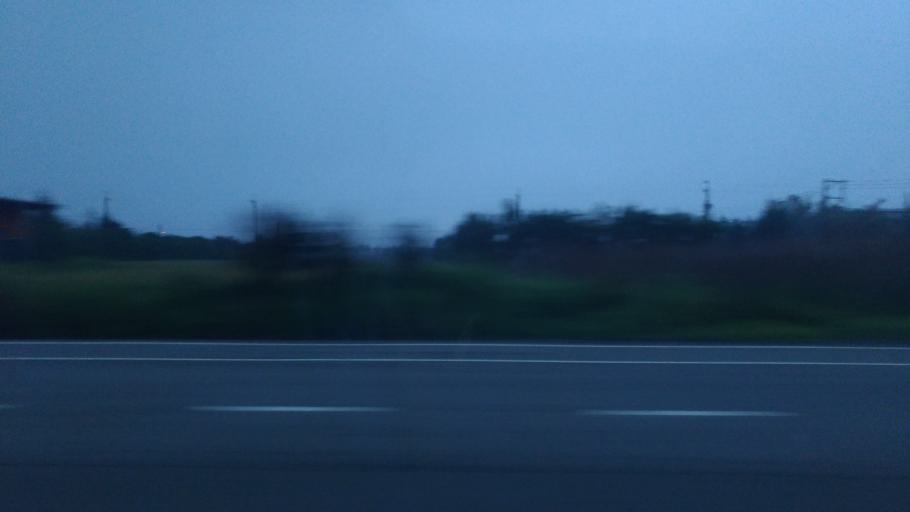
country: TW
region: Taiwan
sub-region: Miaoli
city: Miaoli
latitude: 24.6398
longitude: 120.7857
